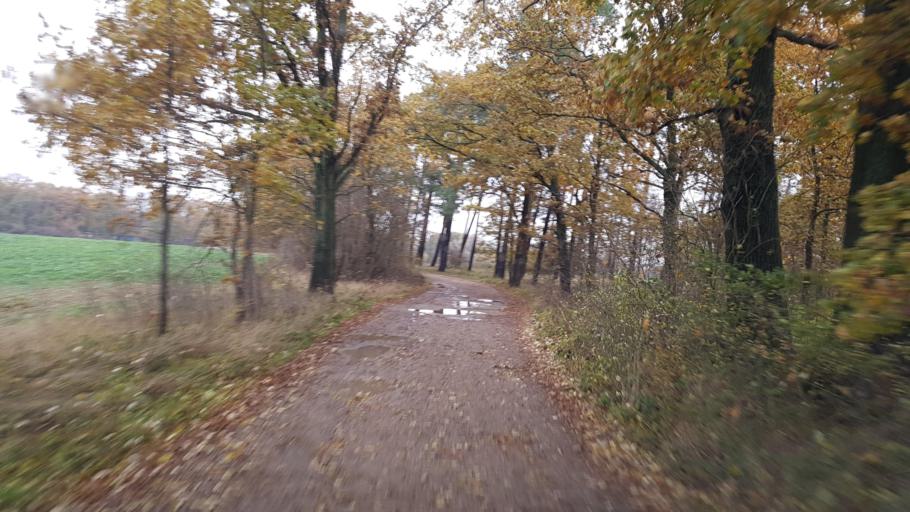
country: DE
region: Brandenburg
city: Drebkau
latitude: 51.6935
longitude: 14.2254
